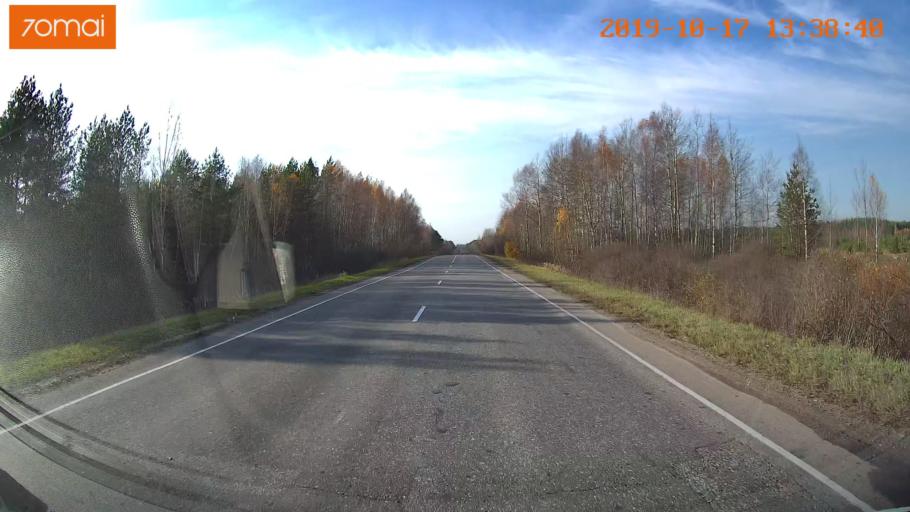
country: RU
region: Rjazan
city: Tuma
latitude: 55.1444
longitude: 40.6075
